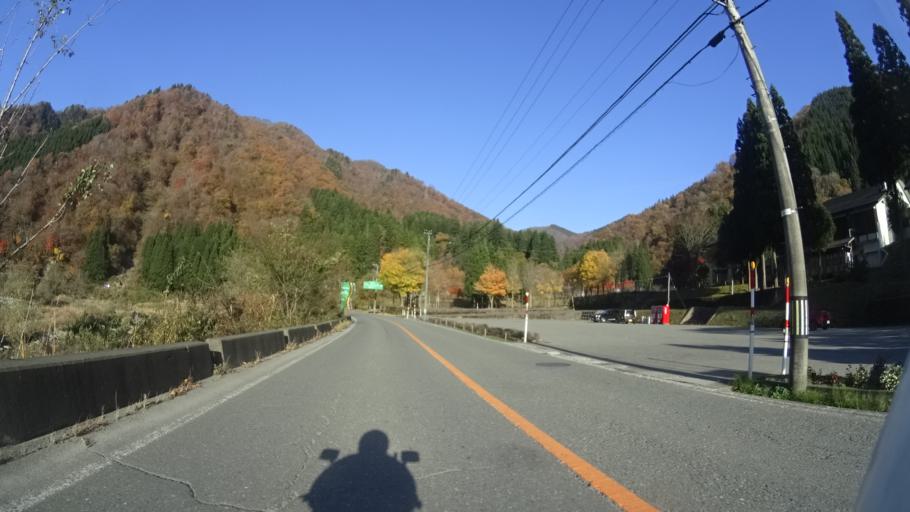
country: JP
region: Fukui
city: Ono
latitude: 35.9224
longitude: 136.6441
